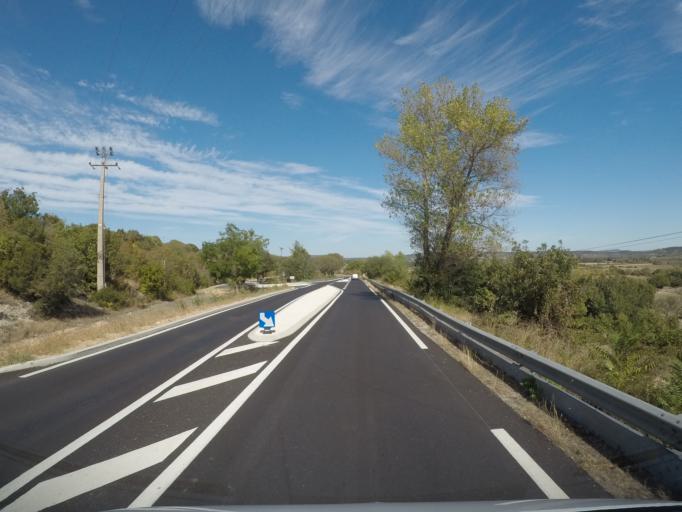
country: FR
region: Languedoc-Roussillon
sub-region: Departement de l'Herault
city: Saint-Martin-de-Londres
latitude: 43.8065
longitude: 3.7398
